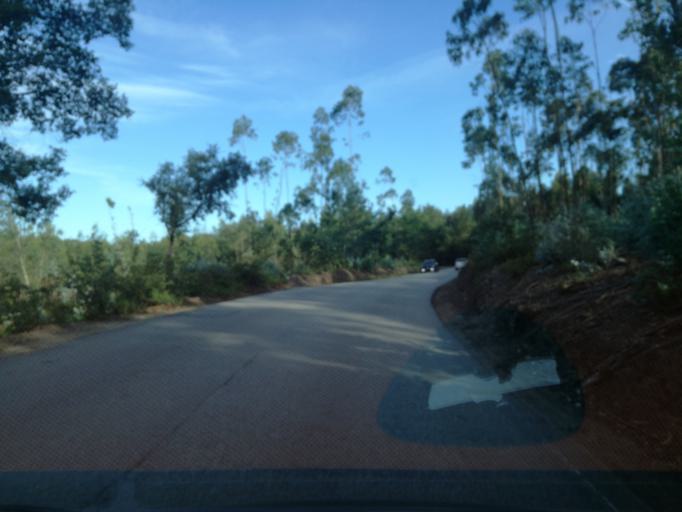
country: PT
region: Porto
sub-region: Valongo
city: Alfena
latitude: 41.2676
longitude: -8.5291
